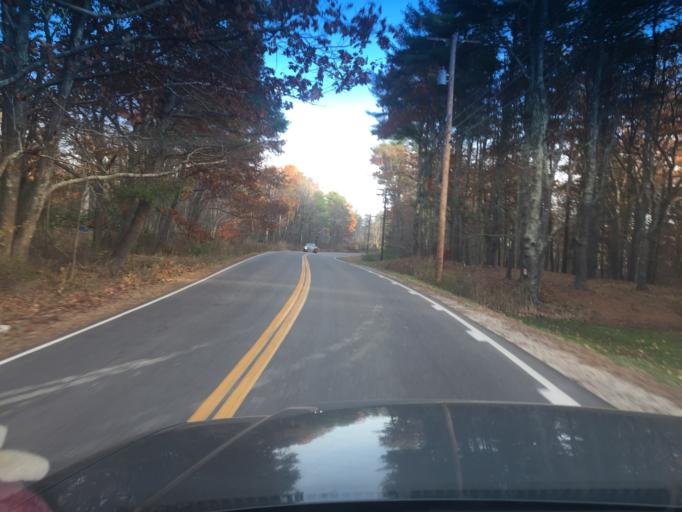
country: US
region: Maine
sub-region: York County
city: York Harbor
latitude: 43.1634
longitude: -70.7085
